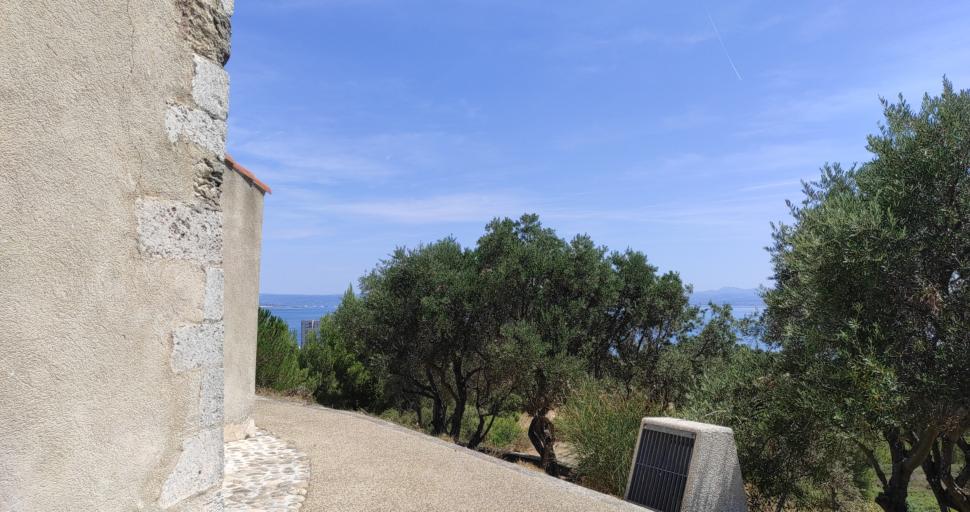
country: FR
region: Provence-Alpes-Cote d'Azur
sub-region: Departement des Bouches-du-Rhone
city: Martigues
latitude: 43.4157
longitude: 5.0463
